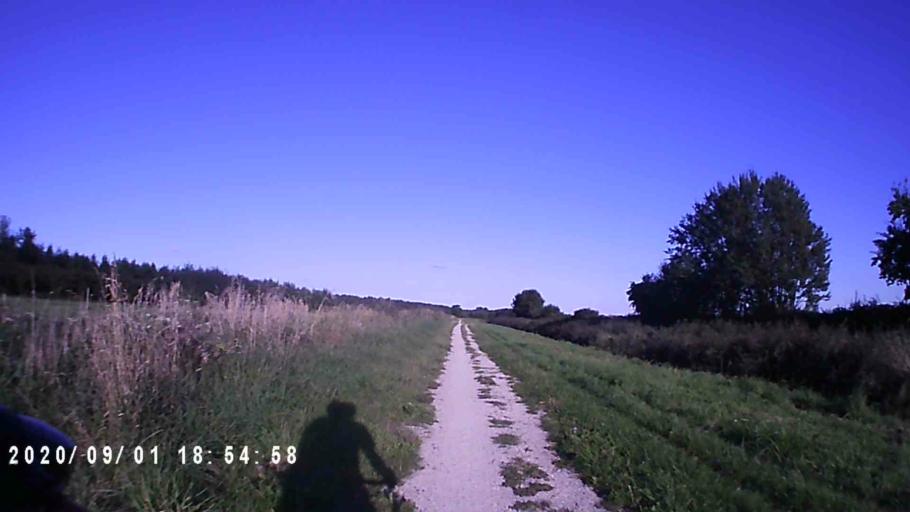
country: NL
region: Groningen
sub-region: Gemeente Veendam
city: Veendam
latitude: 53.1302
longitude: 6.8467
